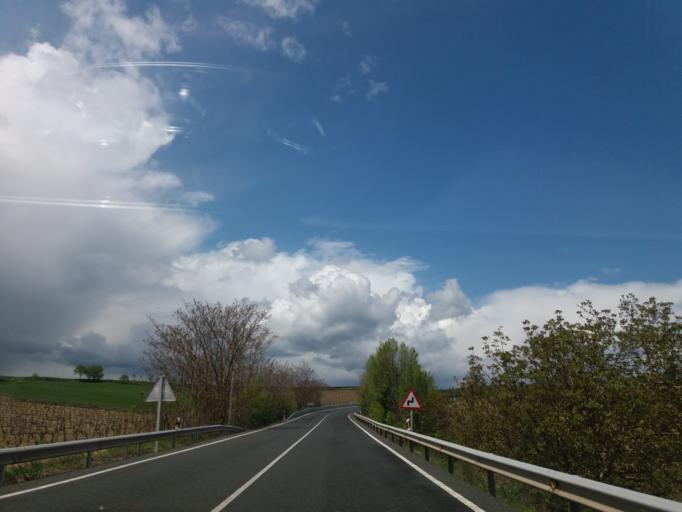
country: ES
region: La Rioja
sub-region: Provincia de La Rioja
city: Fonzaleche
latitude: 42.5788
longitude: -3.0229
